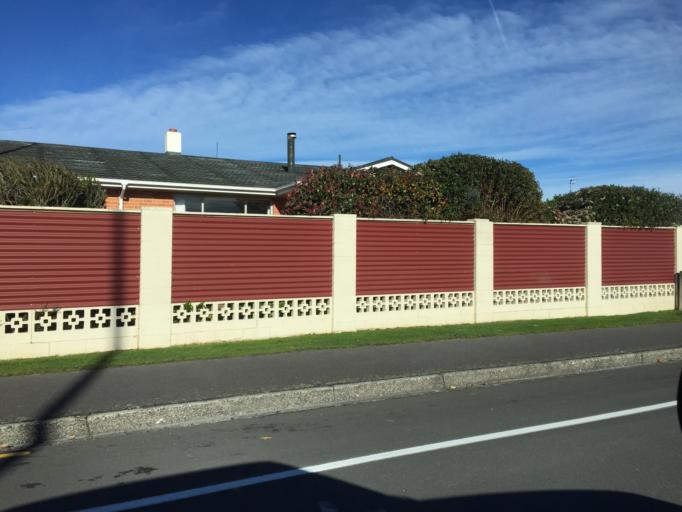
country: NZ
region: Southland
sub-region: Invercargill City
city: Invercargill
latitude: -46.4019
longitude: 168.3701
